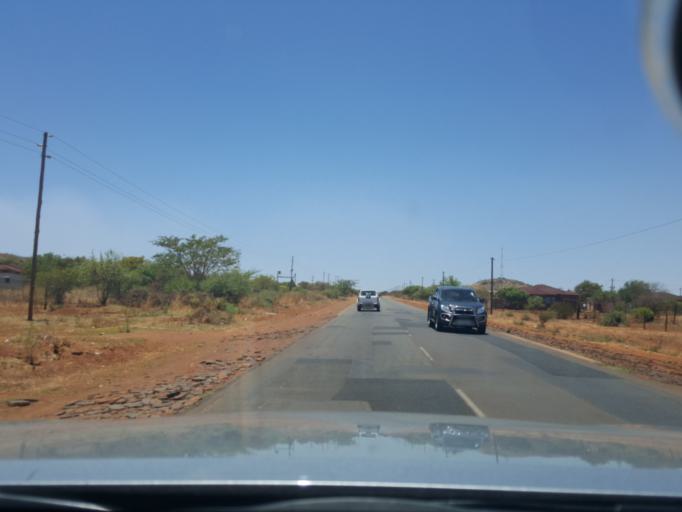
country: ZA
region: North-West
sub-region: Ngaka Modiri Molema District Municipality
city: Zeerust
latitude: -25.4665
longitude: 25.9732
